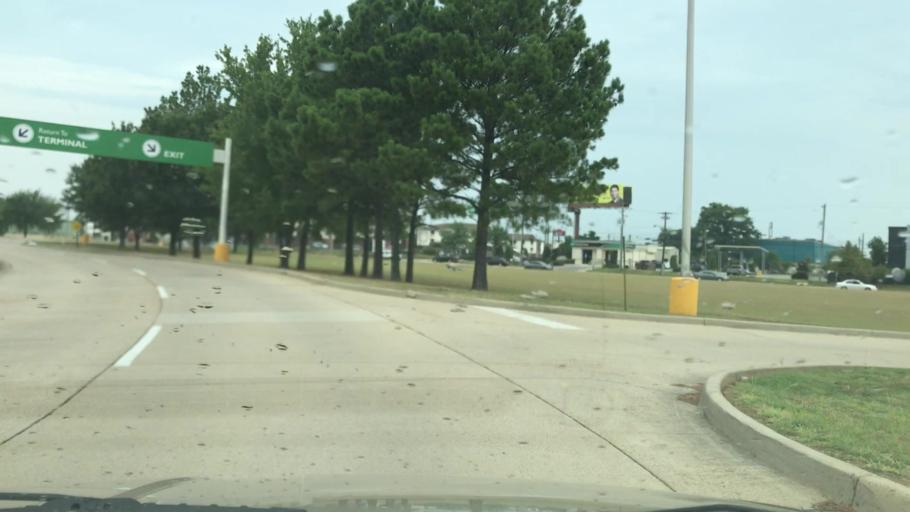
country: US
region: Louisiana
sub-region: Caddo Parish
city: Shreveport
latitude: 32.4556
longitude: -93.8257
